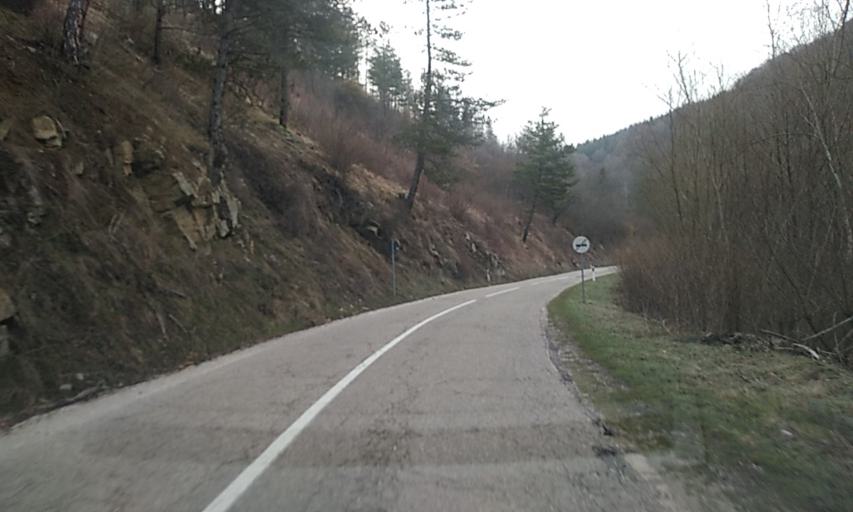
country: RS
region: Central Serbia
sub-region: Pcinjski Okrug
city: Bosilegrad
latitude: 42.5999
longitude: 22.4040
